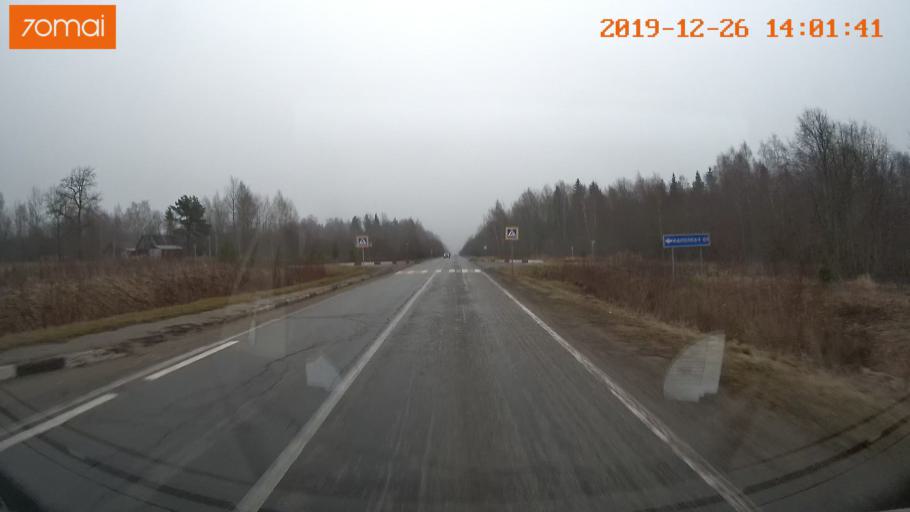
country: RU
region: Jaroslavl
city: Poshekhon'ye
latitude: 58.5487
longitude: 38.7685
